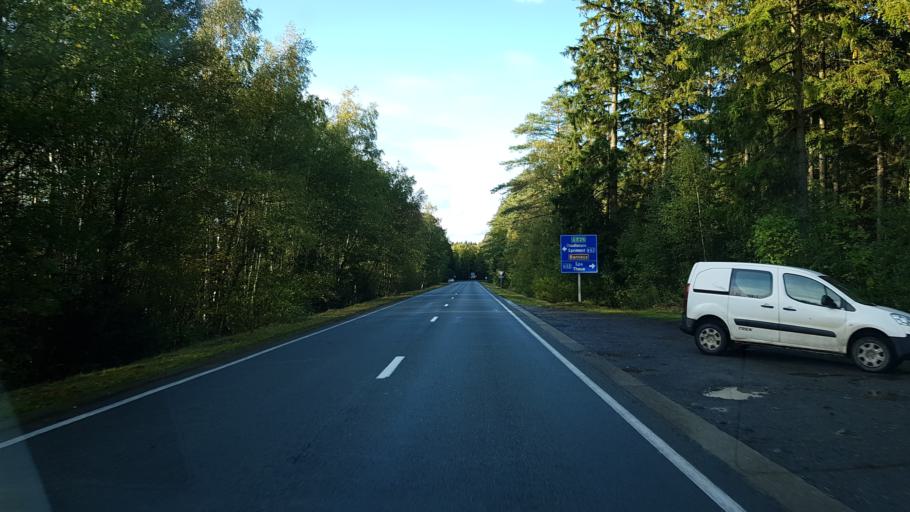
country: BE
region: Wallonia
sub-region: Province de Liege
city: Theux
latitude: 50.5297
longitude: 5.7636
